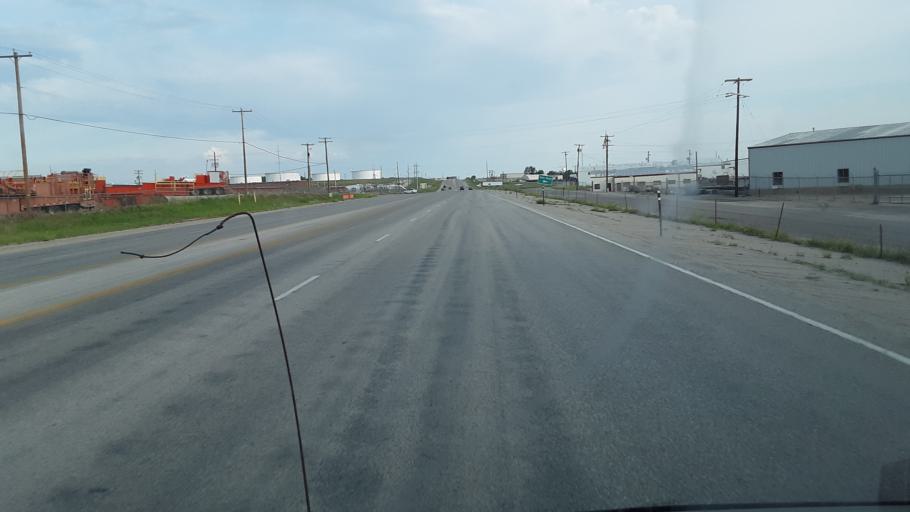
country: US
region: Wyoming
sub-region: Natrona County
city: Mills
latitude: 42.8625
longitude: -106.4035
